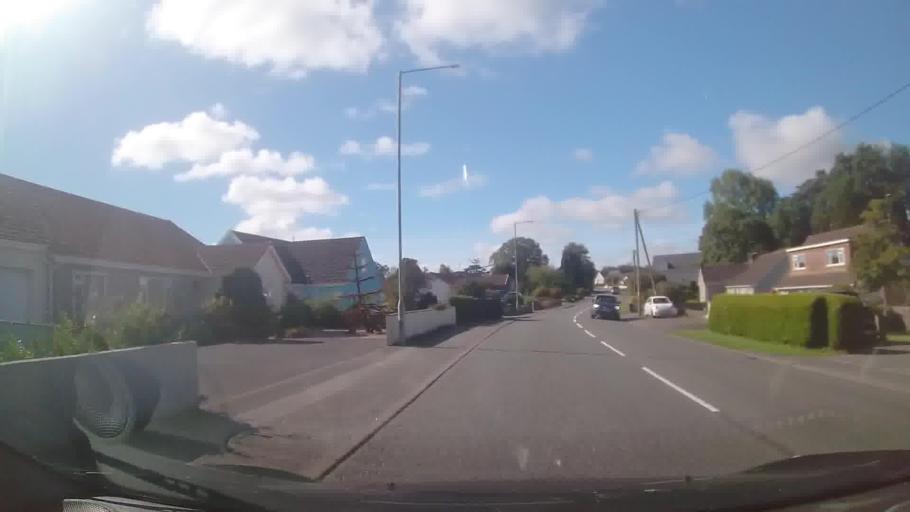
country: GB
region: Wales
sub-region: Pembrokeshire
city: Kilgetty
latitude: 51.7175
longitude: -4.7316
